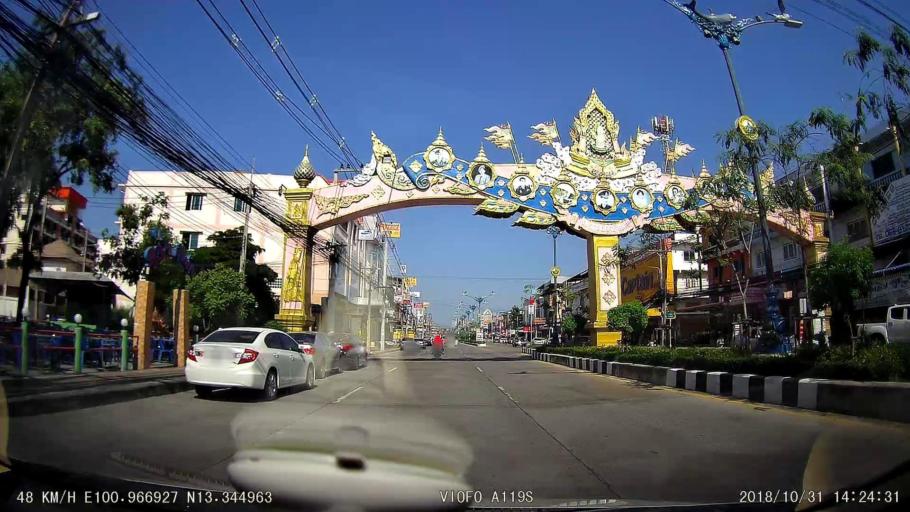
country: TH
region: Chon Buri
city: Chon Buri
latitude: 13.3452
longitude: 100.9673
